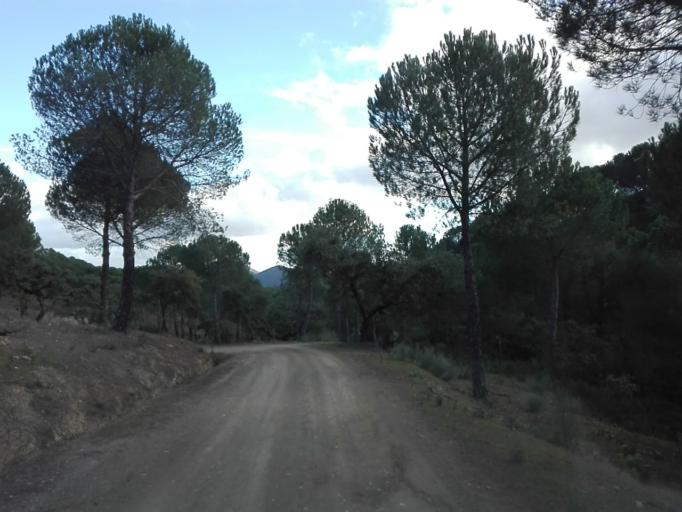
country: ES
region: Extremadura
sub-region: Provincia de Badajoz
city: Casas de Reina
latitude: 38.1789
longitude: -5.9760
